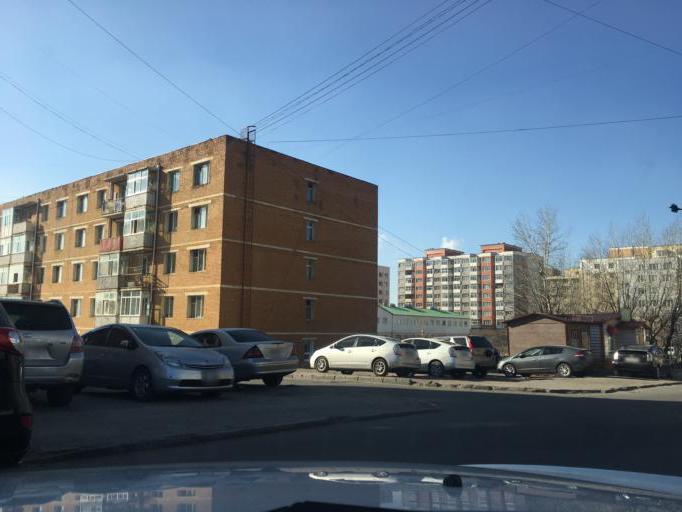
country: MN
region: Ulaanbaatar
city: Ulaanbaatar
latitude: 47.9199
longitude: 106.8703
